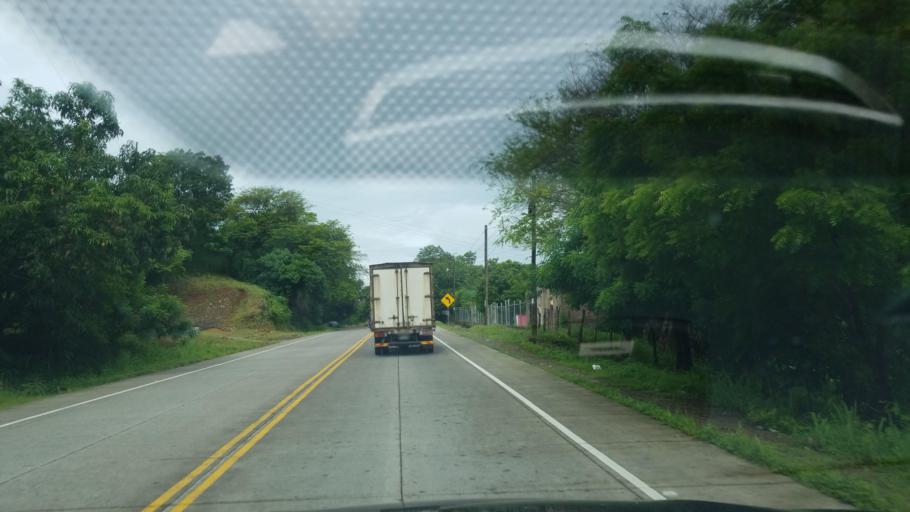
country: HN
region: Francisco Morazan
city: El Porvenir
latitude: 13.6778
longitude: -87.3543
